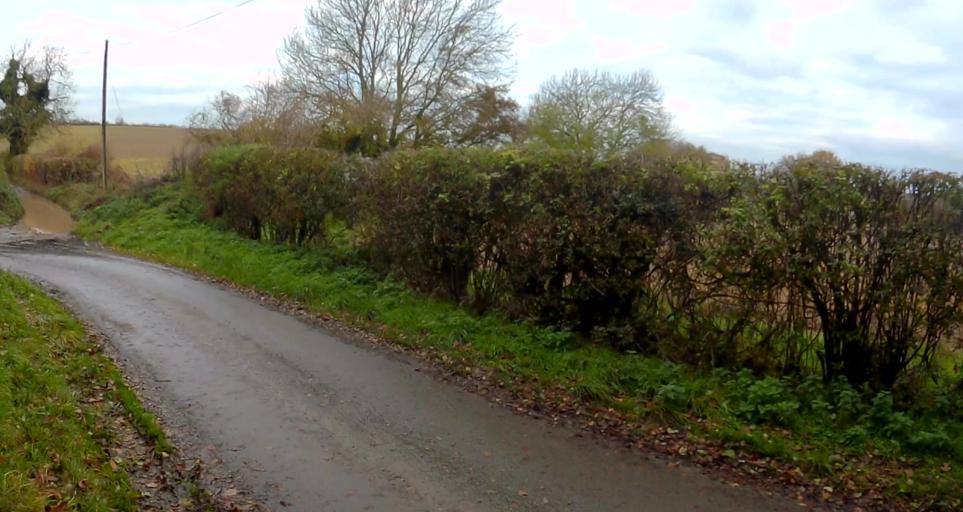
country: GB
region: England
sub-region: Hampshire
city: Long Sutton
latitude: 51.2400
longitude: -0.8906
